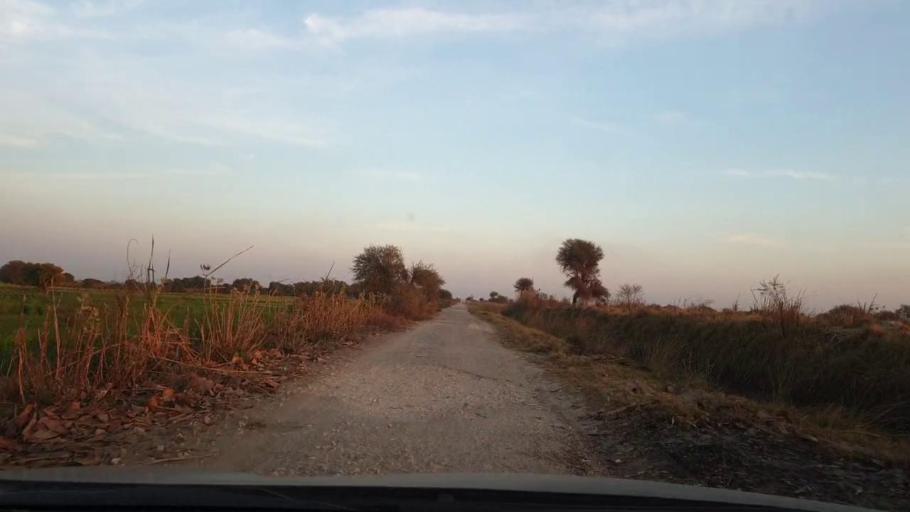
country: PK
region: Sindh
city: Tando Allahyar
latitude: 25.5865
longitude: 68.7184
